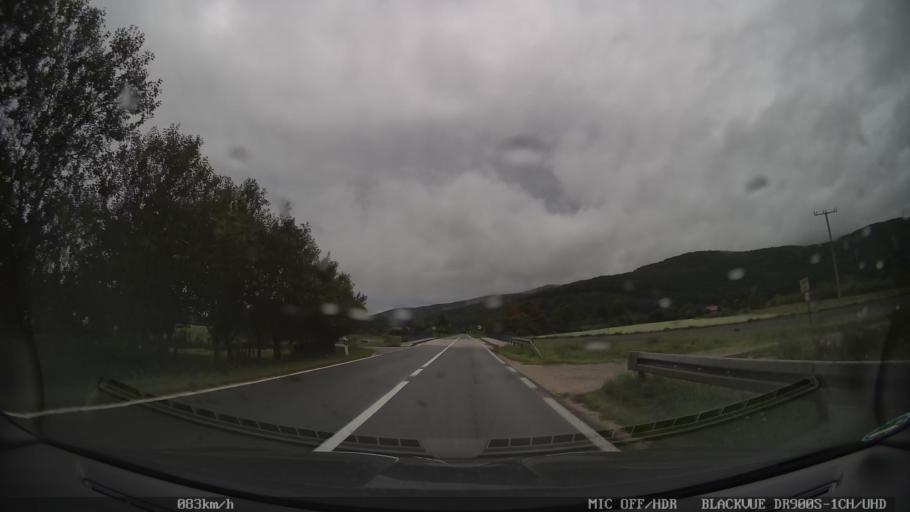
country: HR
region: Licko-Senjska
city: Brinje
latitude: 44.9459
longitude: 15.1262
